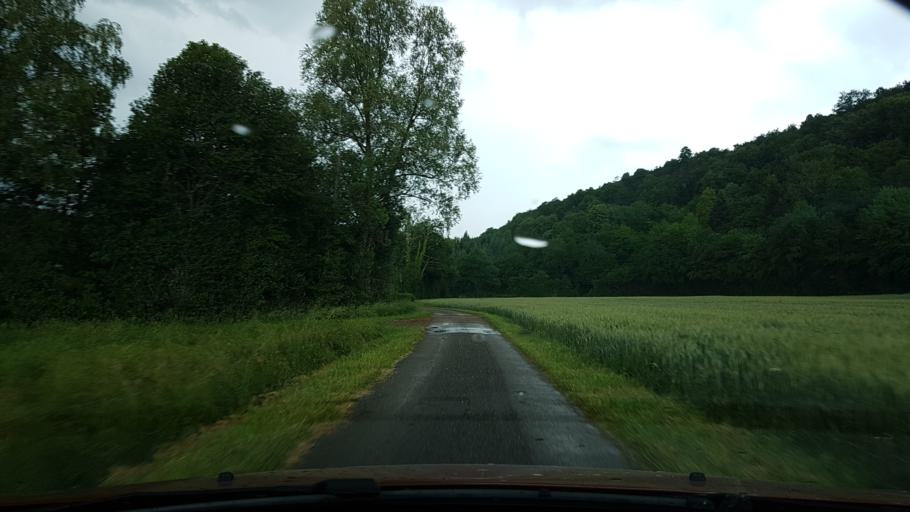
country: FR
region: Franche-Comte
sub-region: Departement du Jura
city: Clairvaux-les-Lacs
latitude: 46.5385
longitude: 5.7038
